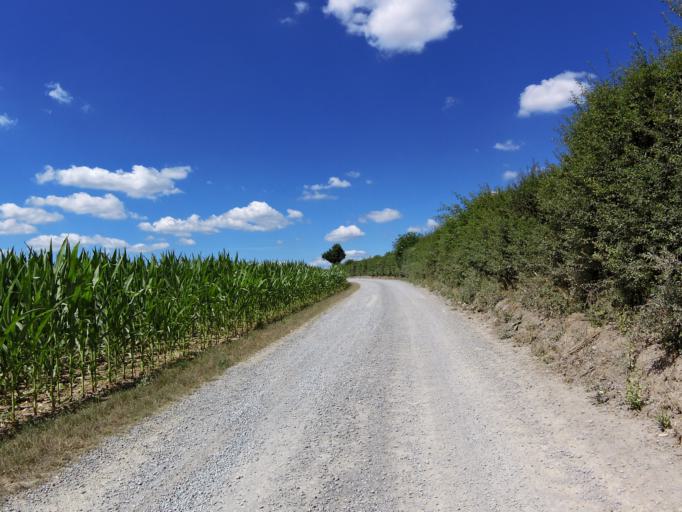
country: DE
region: Bavaria
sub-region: Regierungsbezirk Unterfranken
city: Wuerzburg
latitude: 49.8248
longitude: 9.9473
